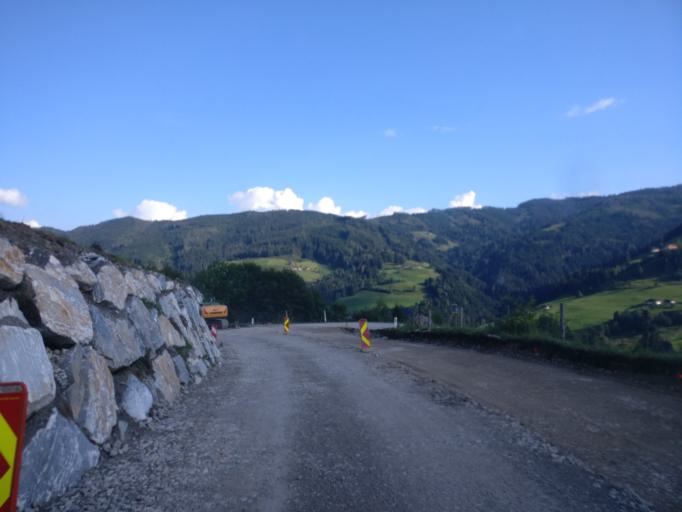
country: AT
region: Salzburg
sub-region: Politischer Bezirk Sankt Johann im Pongau
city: Muhlbach am Hochkonig
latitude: 47.3835
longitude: 13.1230
